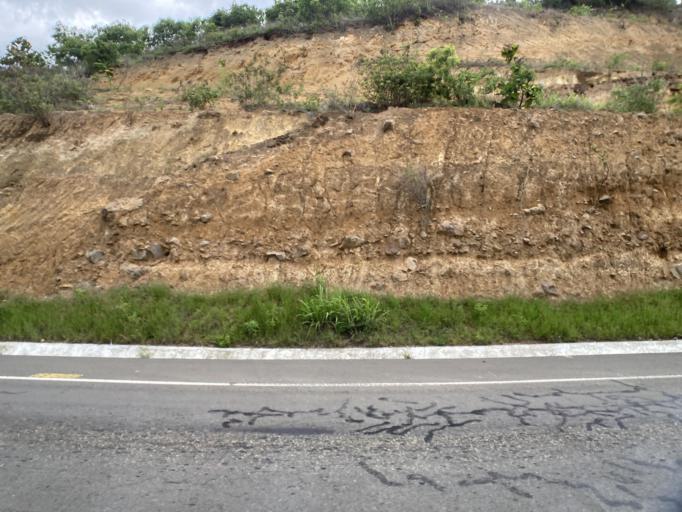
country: GT
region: Sacatepequez
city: Jocotenango
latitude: 14.5818
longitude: -90.7502
